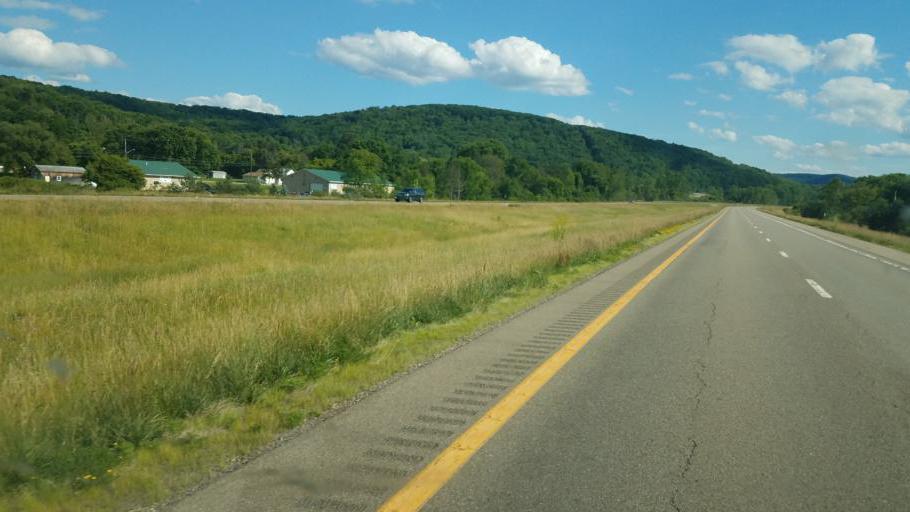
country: US
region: New York
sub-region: Cattaraugus County
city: Olean
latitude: 42.1148
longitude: -78.4182
